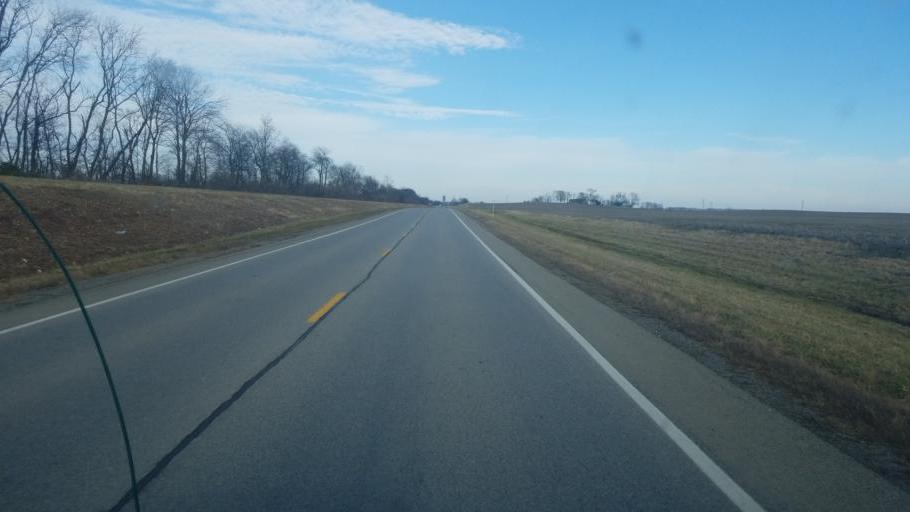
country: US
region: Illinois
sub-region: White County
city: Carmi
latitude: 38.1430
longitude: -88.0862
